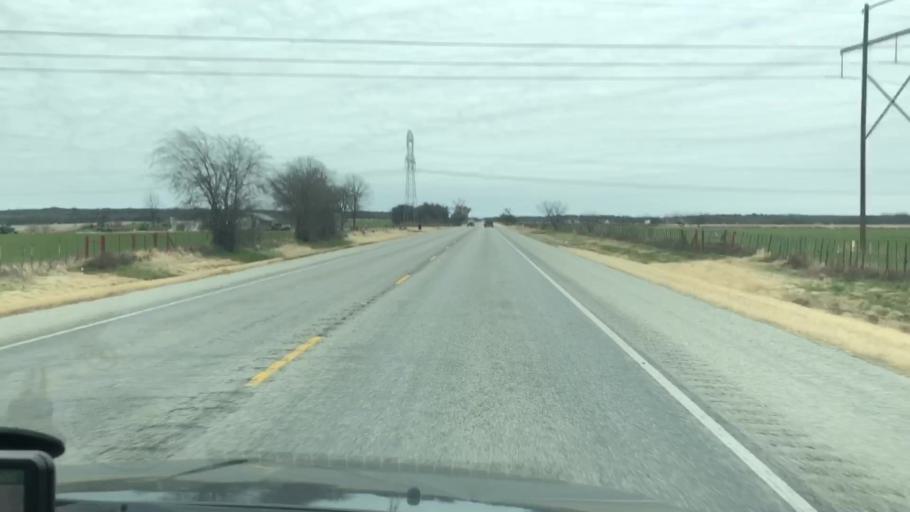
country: US
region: Texas
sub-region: Palo Pinto County
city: Mineral Wells
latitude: 32.9285
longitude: -98.0716
